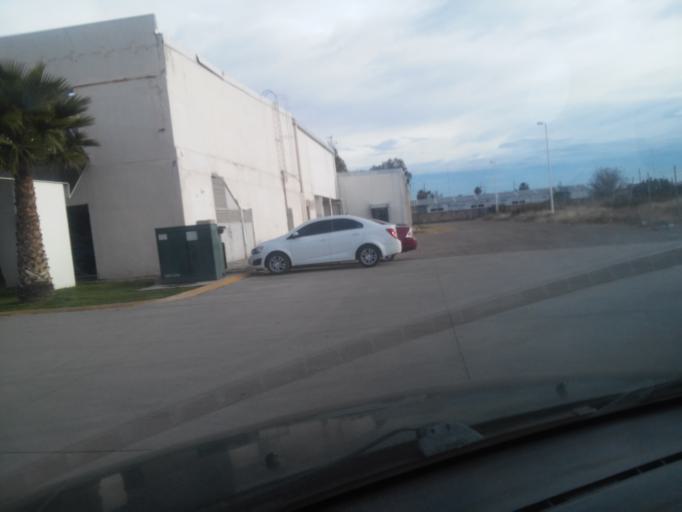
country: MX
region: Durango
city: Victoria de Durango
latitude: 24.0362
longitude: -104.6338
